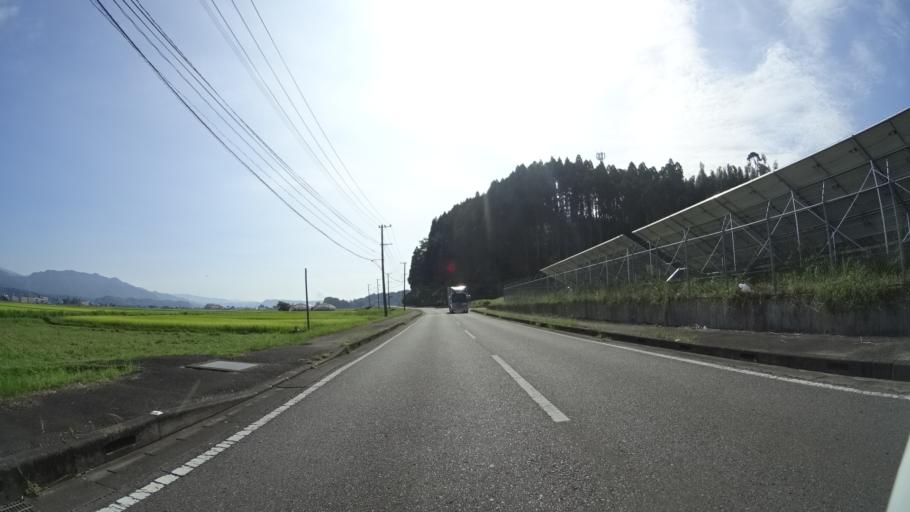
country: JP
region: Kagoshima
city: Okuchi-shinohara
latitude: 32.0395
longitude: 130.8010
